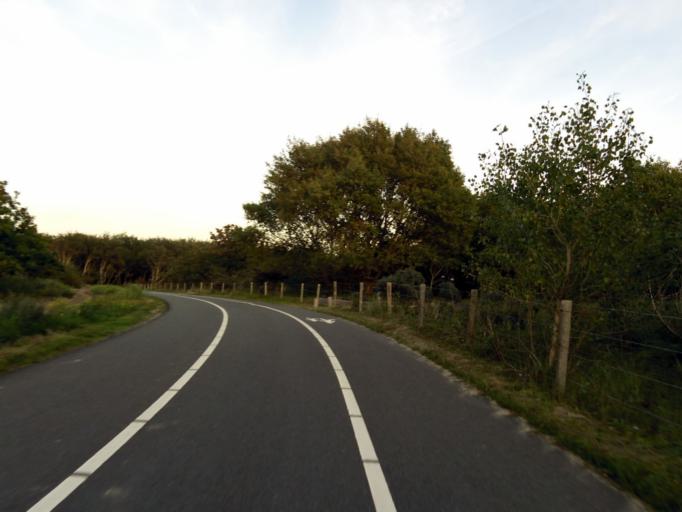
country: NL
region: South Holland
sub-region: Gemeente Wassenaar
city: Wassenaar
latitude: 52.1602
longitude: 4.3679
